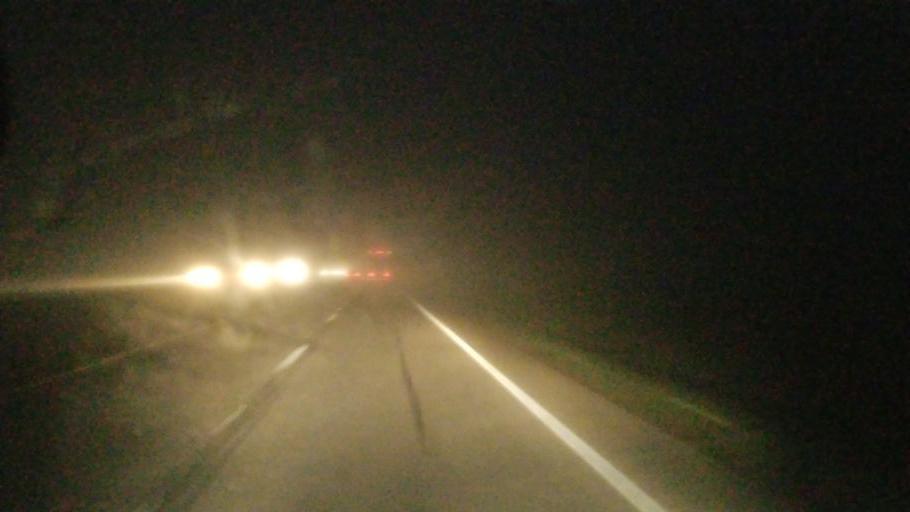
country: US
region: Ohio
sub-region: Pickaway County
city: Logan Elm Village
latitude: 39.5436
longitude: -82.9648
